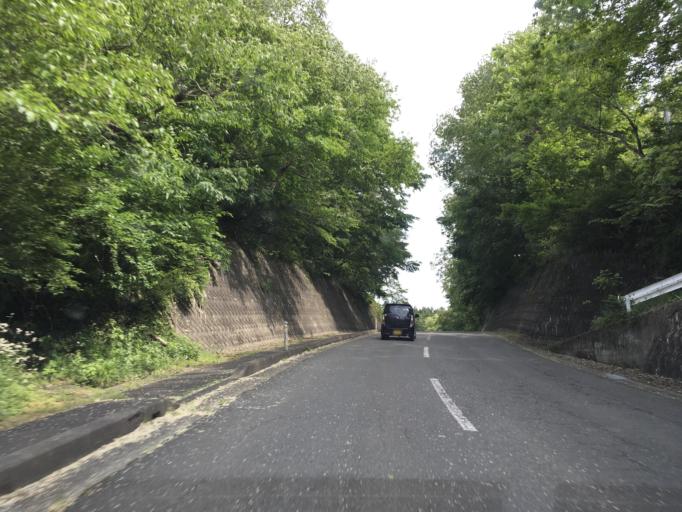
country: JP
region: Iwate
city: Mizusawa
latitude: 39.0655
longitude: 141.3576
